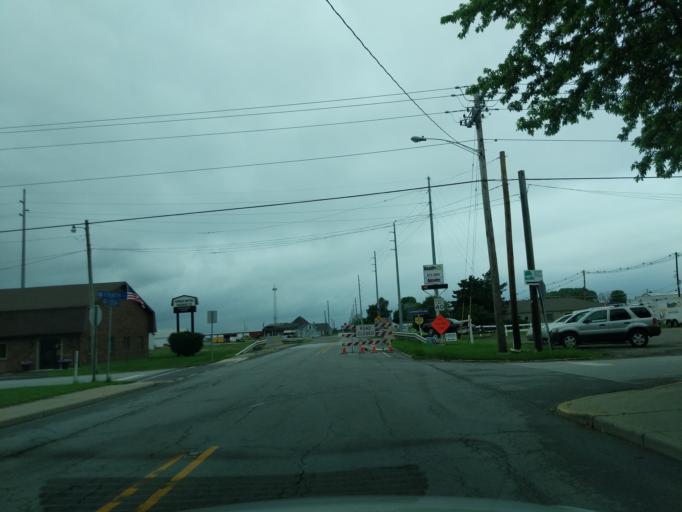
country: US
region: Indiana
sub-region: Tipton County
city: Tipton
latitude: 40.2820
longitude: -86.0496
